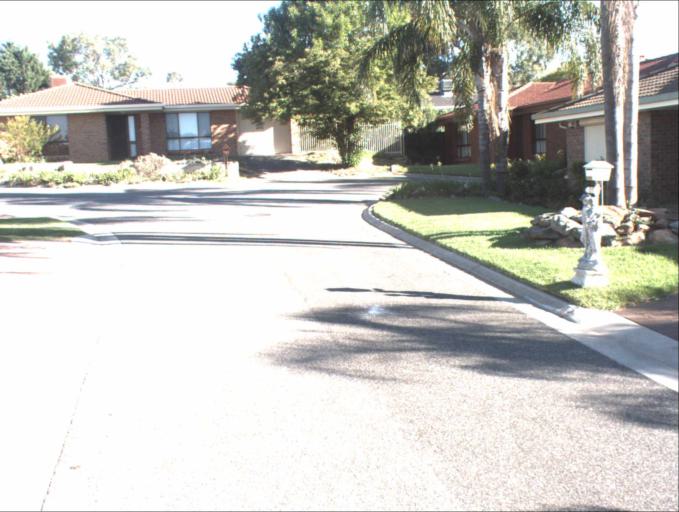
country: AU
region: South Australia
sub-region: Campbelltown
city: Paradise
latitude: -34.8716
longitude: 138.6536
